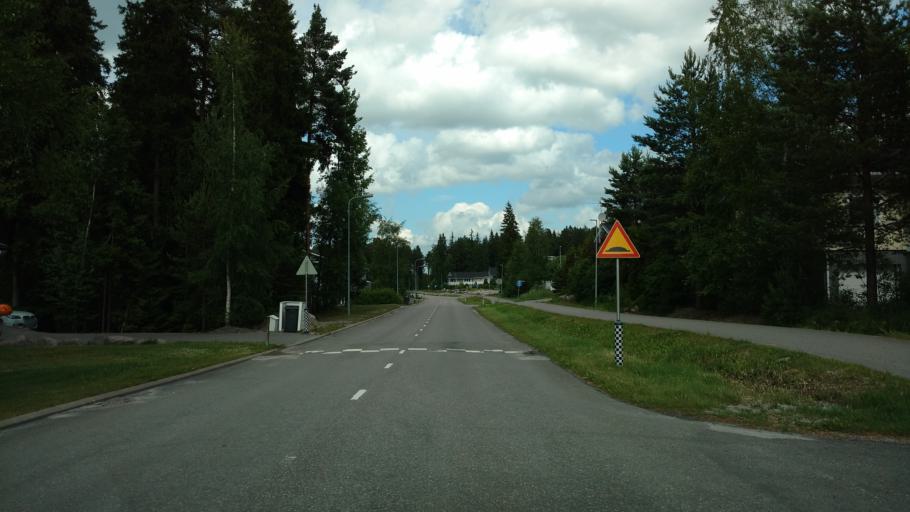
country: FI
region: Varsinais-Suomi
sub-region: Salo
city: Salo
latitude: 60.4034
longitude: 23.1812
